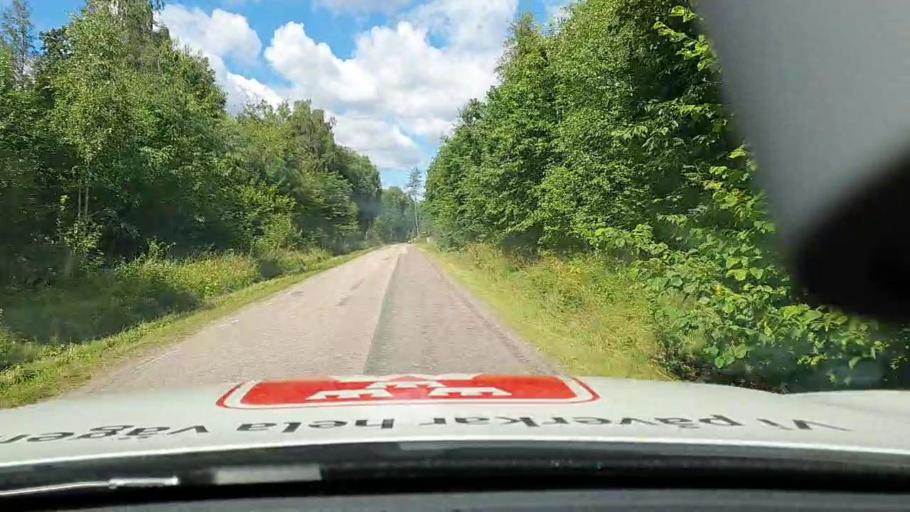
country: SE
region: Vaestra Goetaland
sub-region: Karlsborgs Kommun
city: Molltorp
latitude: 58.5940
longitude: 14.2641
